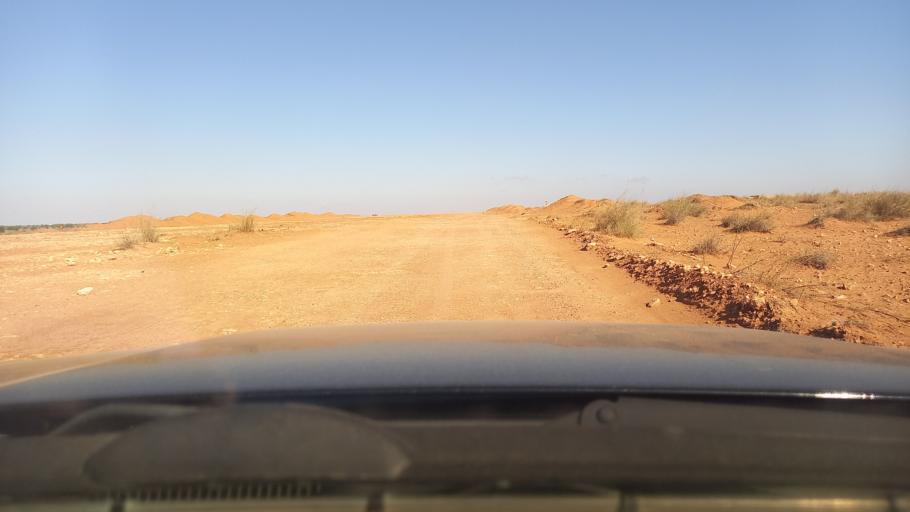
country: TN
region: Madanin
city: Medenine
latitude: 33.1732
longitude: 10.5273
